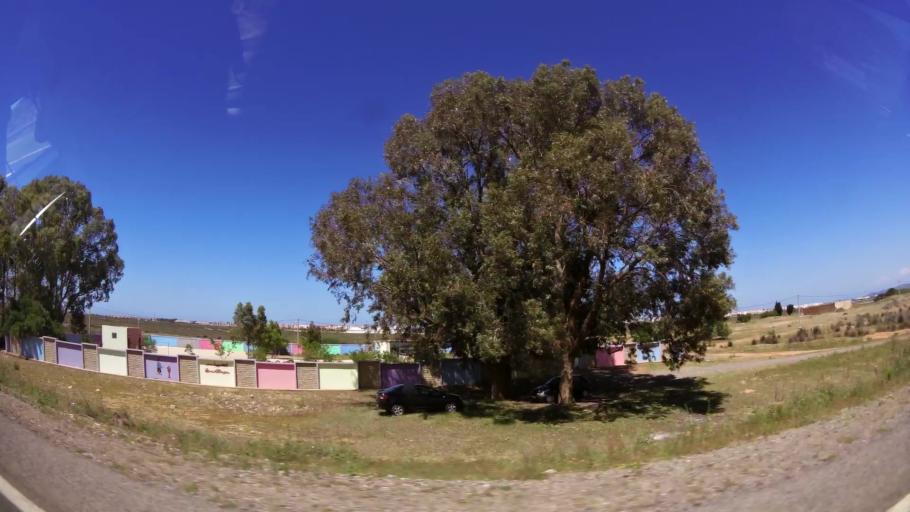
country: MA
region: Oriental
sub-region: Berkane-Taourirt
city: Madagh
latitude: 35.0955
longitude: -2.3169
